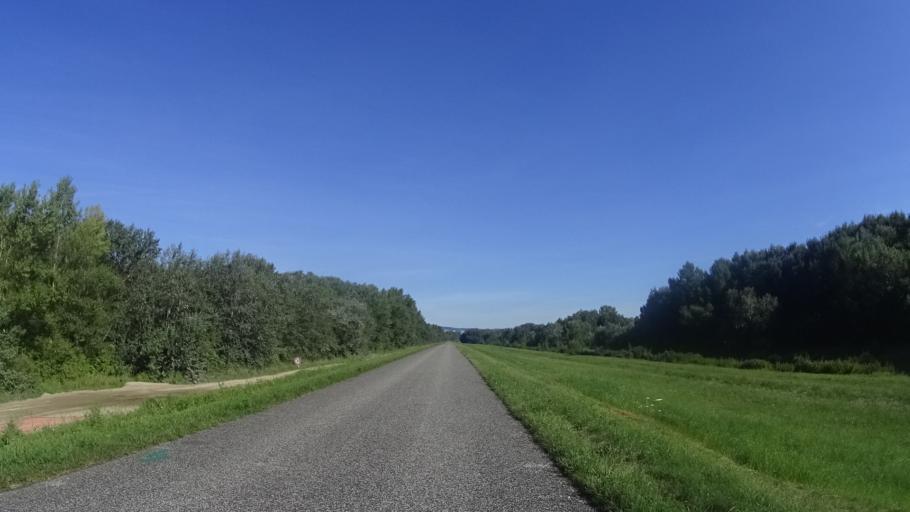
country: SK
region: Bratislavsky
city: Bratislava
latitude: 48.0900
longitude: 17.1544
